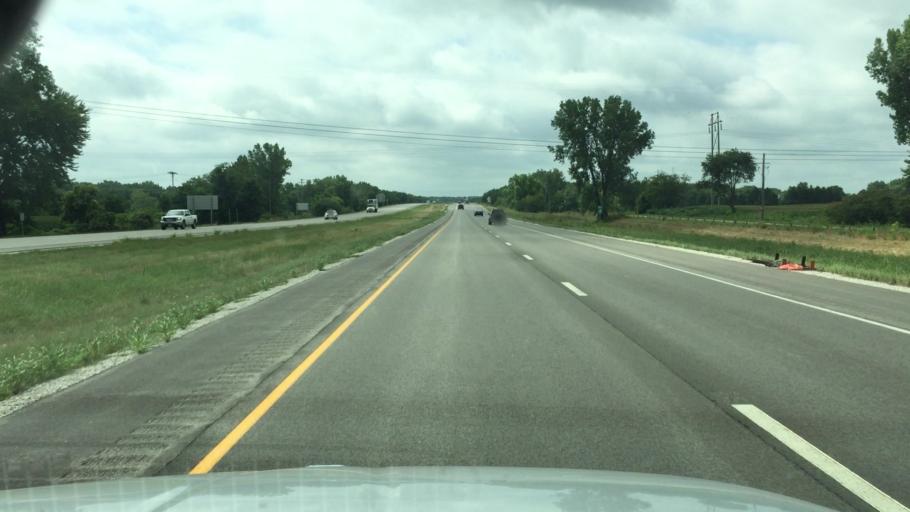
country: US
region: Illinois
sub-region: Henry County
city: Colona
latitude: 41.5287
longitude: -90.3417
